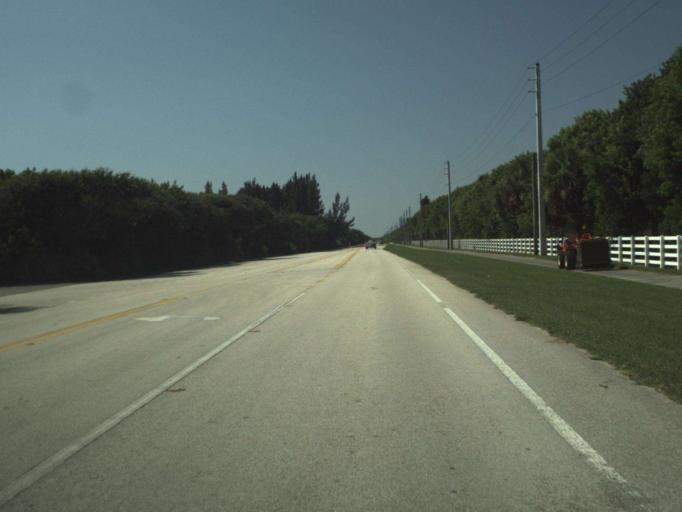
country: US
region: Florida
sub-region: Indian River County
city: Wabasso Beach
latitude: 27.7821
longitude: -80.4079
